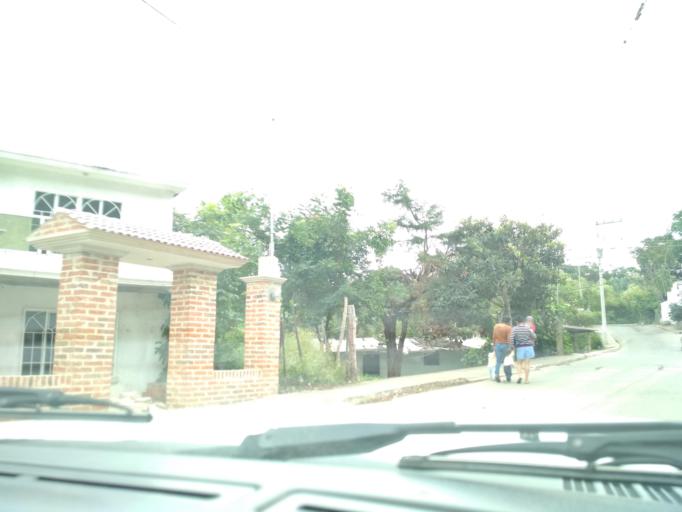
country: MX
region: Veracruz
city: El Castillo
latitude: 19.5782
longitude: -96.8659
